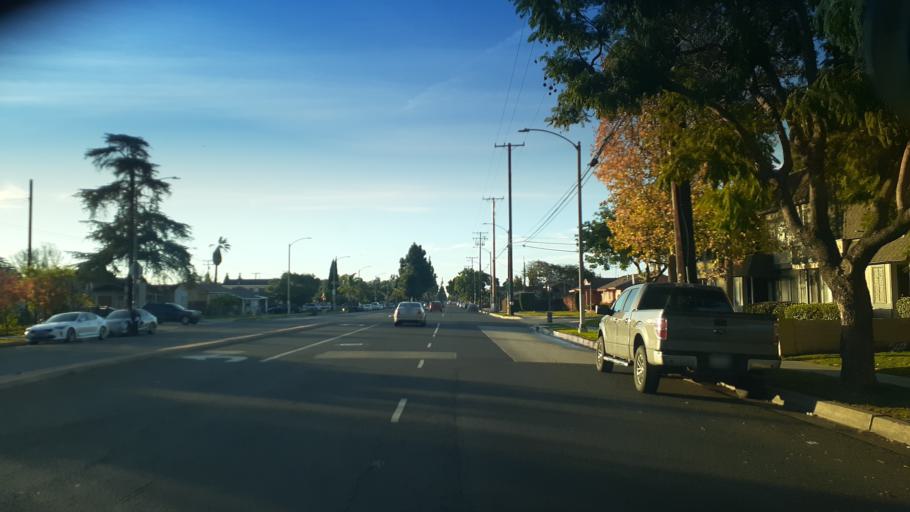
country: US
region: California
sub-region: Los Angeles County
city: Hawaiian Gardens
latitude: 33.8429
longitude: -118.0821
